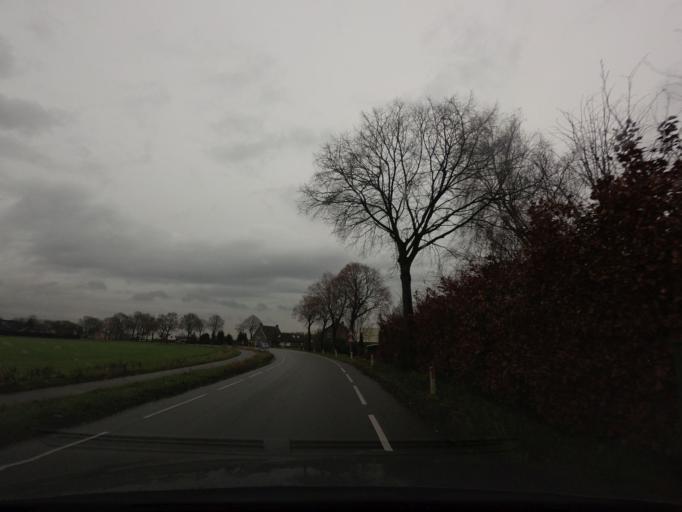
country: NL
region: North Brabant
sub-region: Gemeente Breda
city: Breda
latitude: 51.6067
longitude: 4.6832
